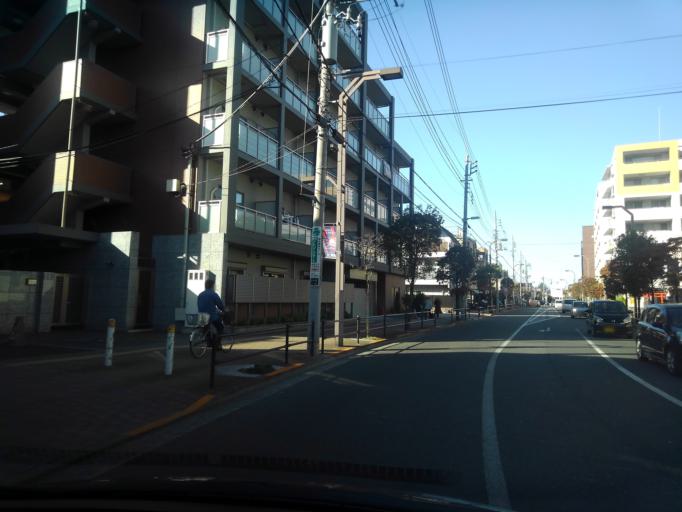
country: JP
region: Tokyo
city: Chofugaoka
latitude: 35.6508
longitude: 139.5569
